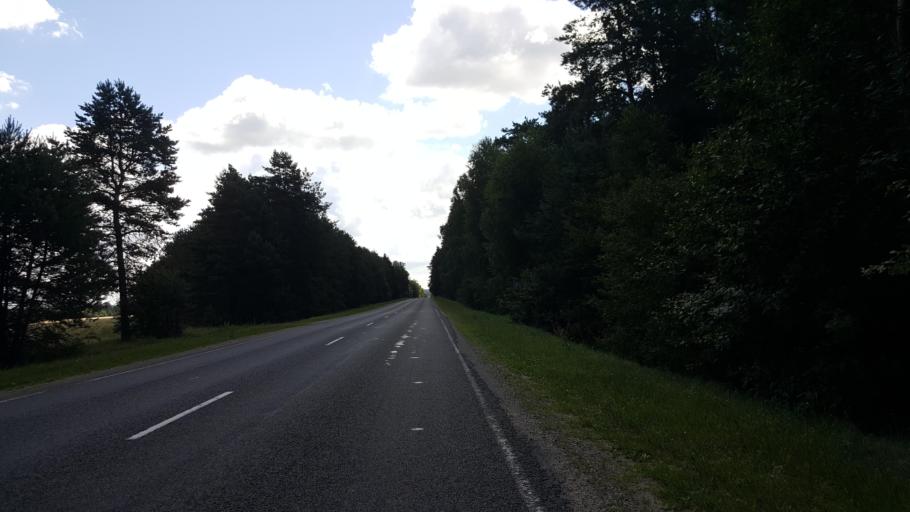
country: BY
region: Brest
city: Kamyanyets
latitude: 52.3789
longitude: 23.8686
